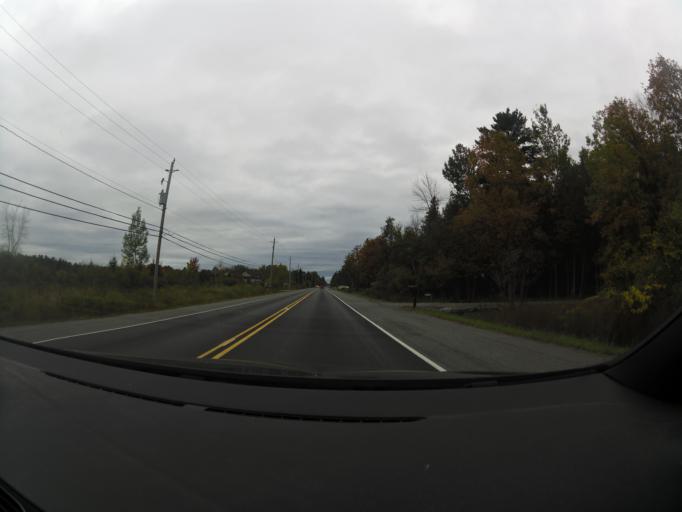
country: CA
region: Ontario
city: Bells Corners
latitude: 45.3816
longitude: -75.9676
